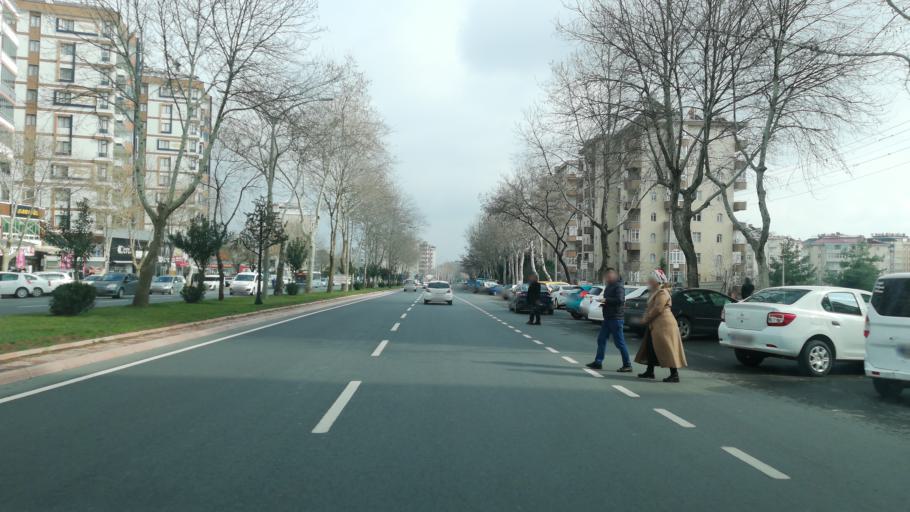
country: TR
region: Kahramanmaras
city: Kahramanmaras
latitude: 37.5871
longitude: 36.8944
